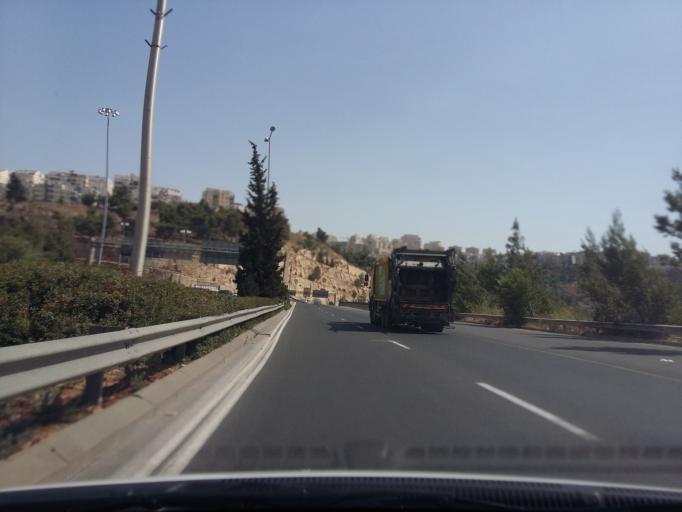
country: IL
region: Jerusalem
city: West Jerusalem
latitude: 31.8037
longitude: 35.2048
